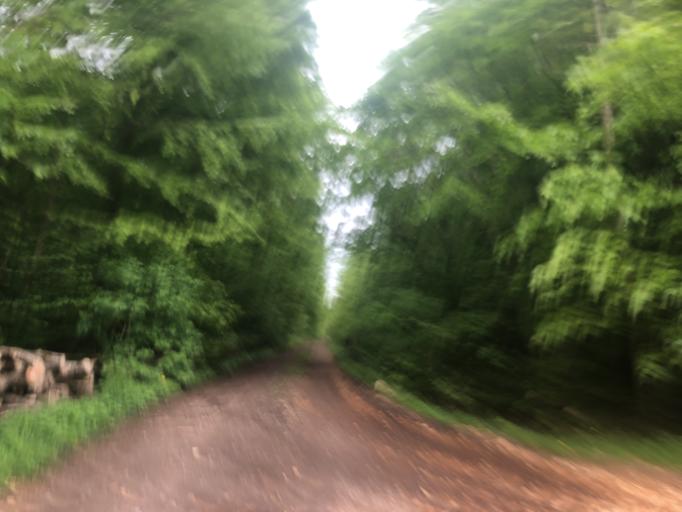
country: DK
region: Zealand
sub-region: Koge Kommune
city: Bjaeverskov
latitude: 55.4332
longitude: 12.0820
